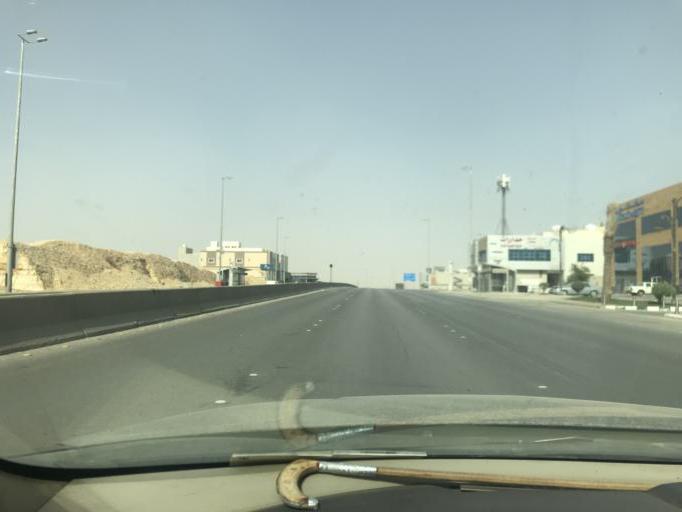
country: SA
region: Ar Riyad
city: Riyadh
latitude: 24.8160
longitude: 46.6835
